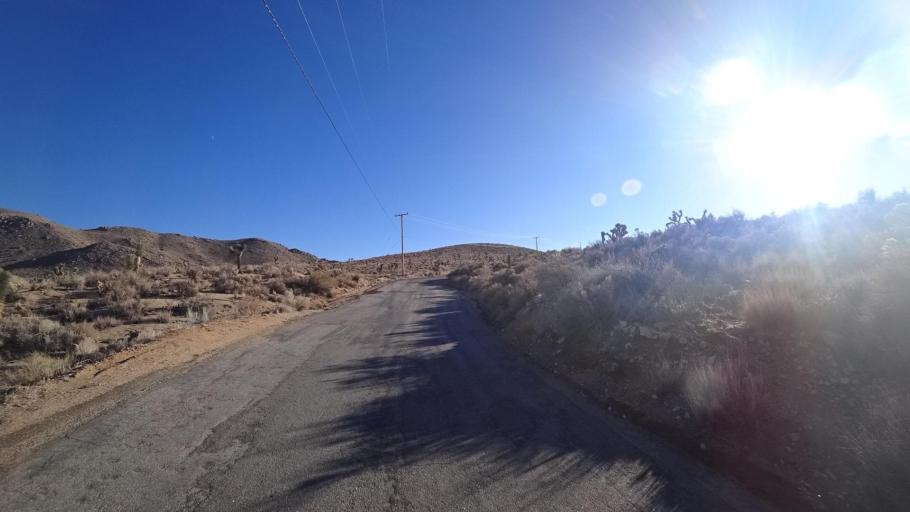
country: US
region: California
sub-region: Kern County
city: Weldon
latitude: 35.5238
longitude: -118.2011
